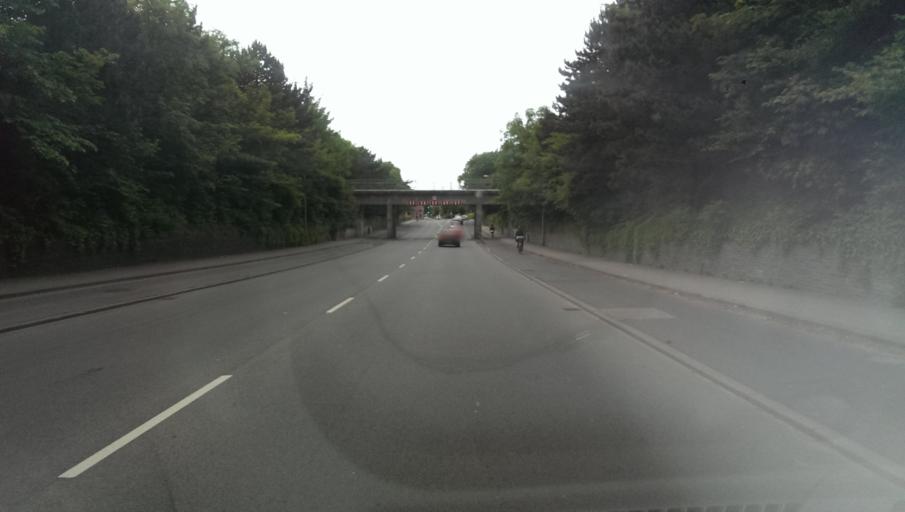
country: DK
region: South Denmark
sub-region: Esbjerg Kommune
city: Esbjerg
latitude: 55.4796
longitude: 8.4647
